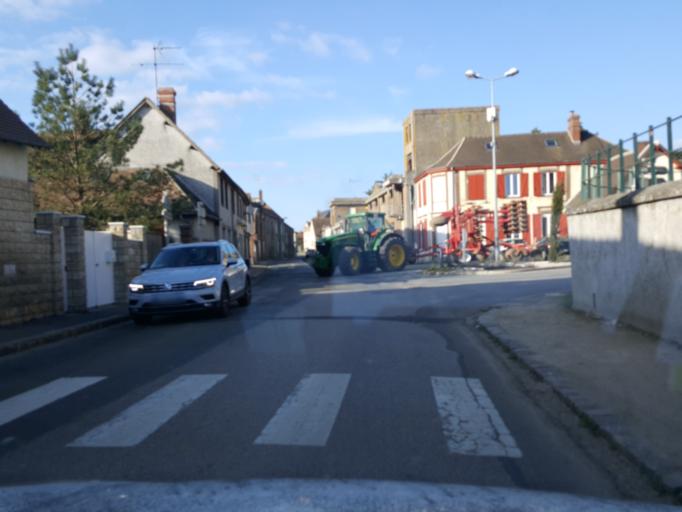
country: FR
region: Centre
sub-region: Departement d'Eure-et-Loir
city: Bu
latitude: 48.7480
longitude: 1.5228
